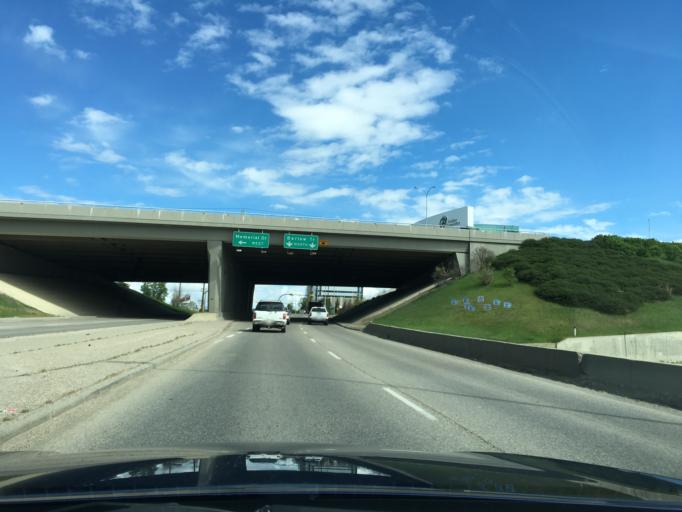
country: CA
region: Alberta
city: Calgary
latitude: 51.0443
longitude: -114.0019
